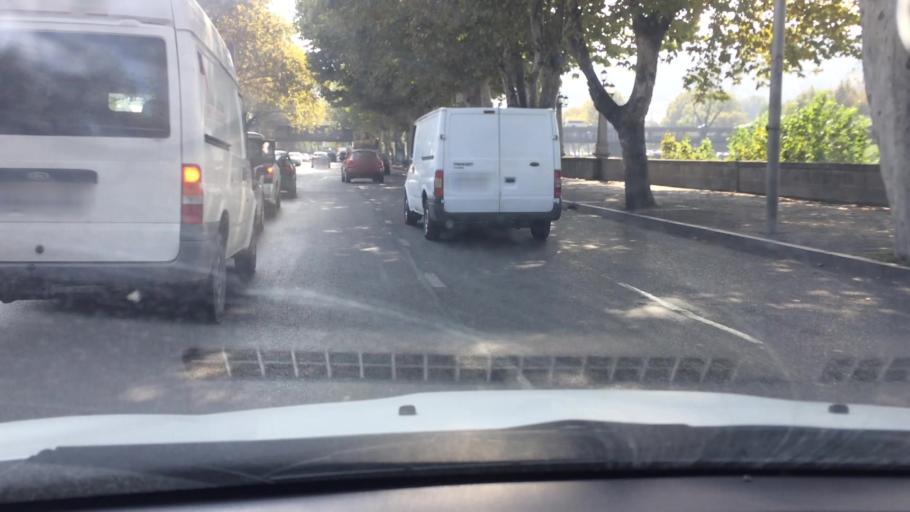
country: GE
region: T'bilisi
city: Tbilisi
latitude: 41.6988
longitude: 44.8086
